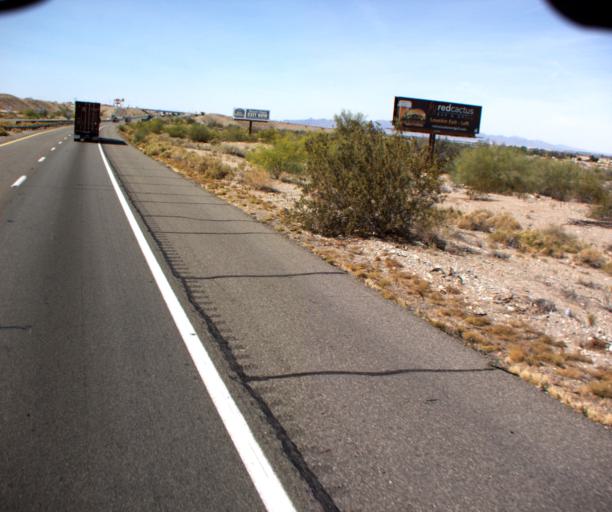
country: US
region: Arizona
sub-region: La Paz County
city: Ehrenberg
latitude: 33.6031
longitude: -114.5091
